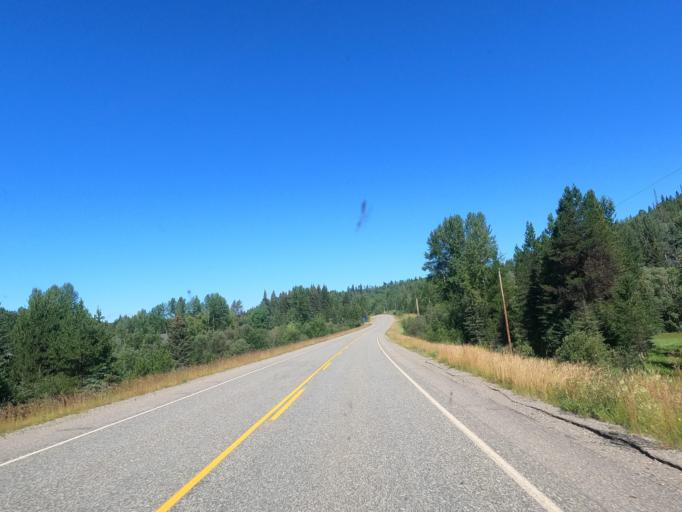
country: CA
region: British Columbia
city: Quesnel
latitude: 53.0490
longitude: -122.1514
